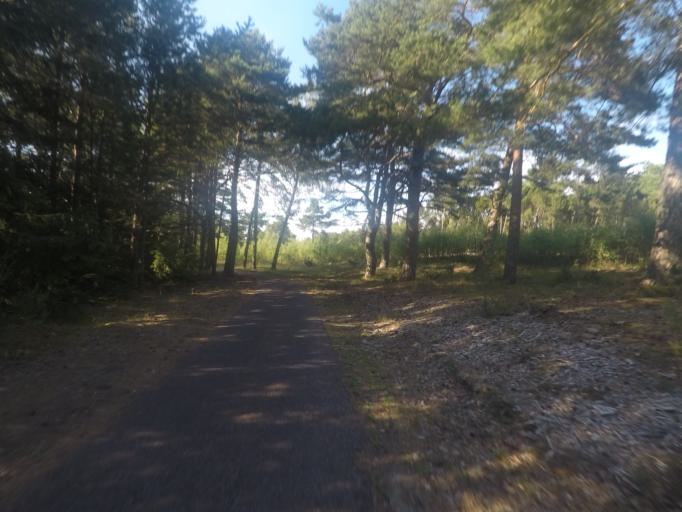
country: LT
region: Klaipedos apskritis
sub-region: Klaipeda
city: Klaipeda
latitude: 55.6038
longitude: 21.1184
